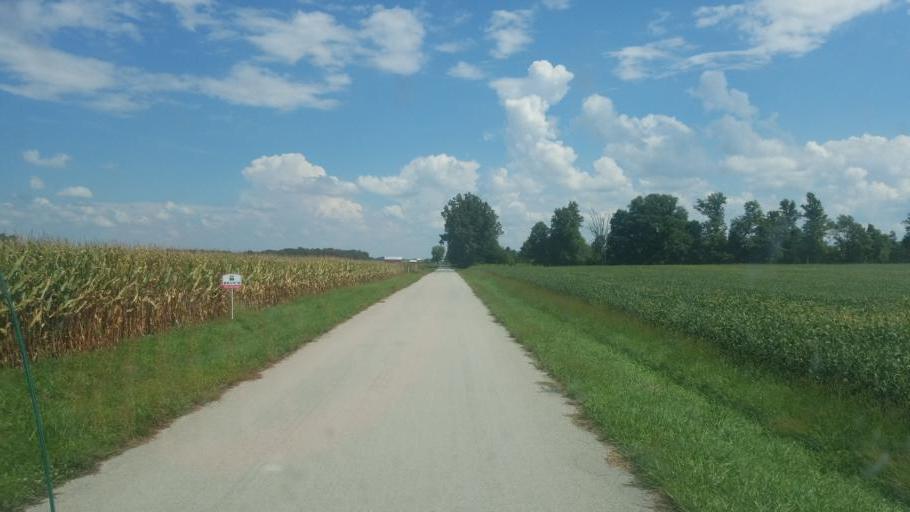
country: US
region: Ohio
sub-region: Hardin County
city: Forest
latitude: 40.8469
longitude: -83.4309
